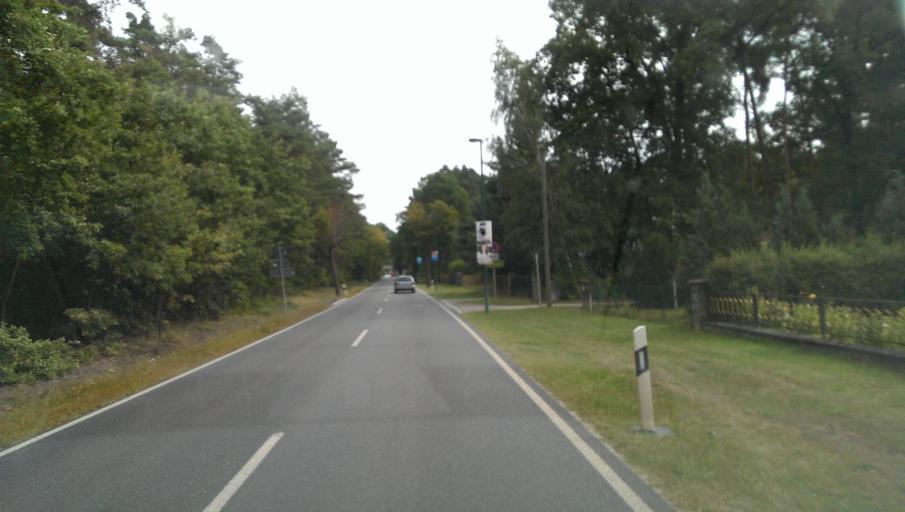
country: DE
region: Brandenburg
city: Am Mellensee
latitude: 52.2253
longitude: 13.3988
